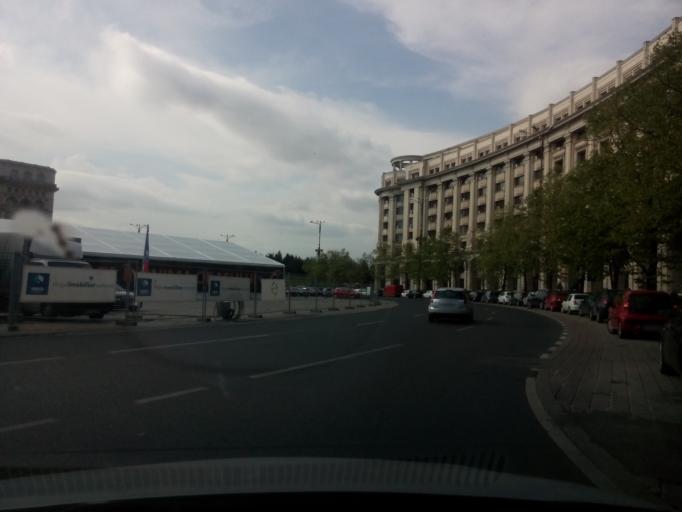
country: RO
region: Bucuresti
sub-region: Municipiul Bucuresti
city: Bucuresti
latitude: 44.4275
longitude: 26.0925
